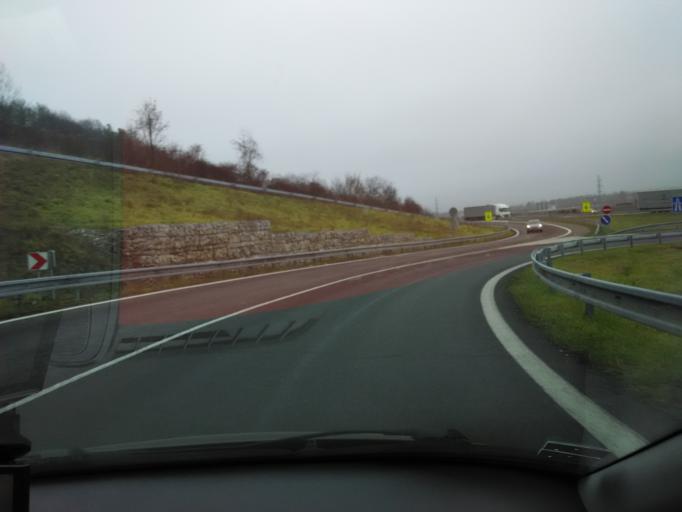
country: SK
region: Trenciansky
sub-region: Okres Trencin
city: Trencin
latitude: 48.9053
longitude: 17.9906
